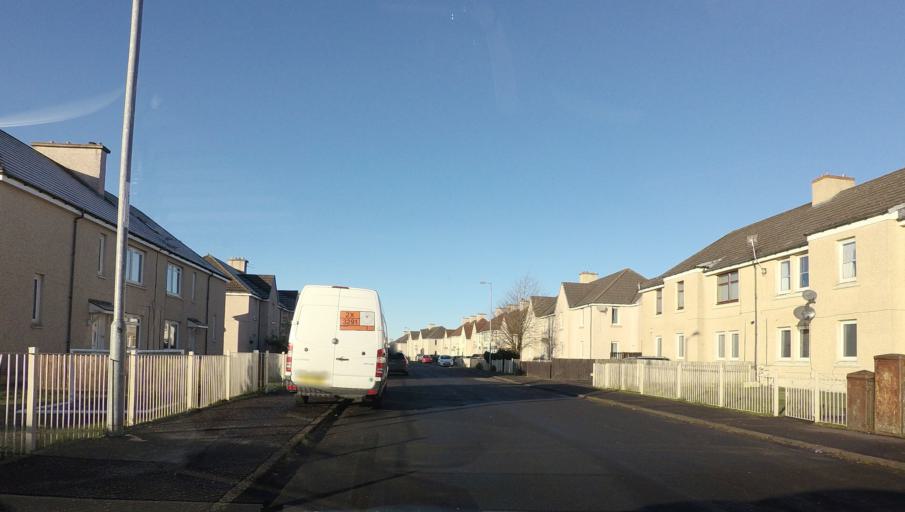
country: GB
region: Scotland
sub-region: North Lanarkshire
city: Newmains
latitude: 55.7870
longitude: -3.8723
